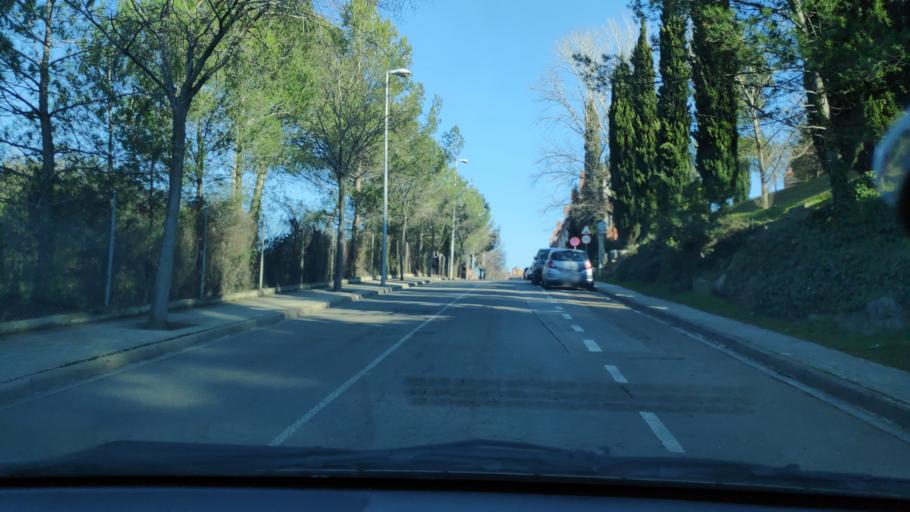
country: ES
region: Catalonia
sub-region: Provincia de Barcelona
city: Sant Cugat del Valles
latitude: 41.4597
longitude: 2.0727
